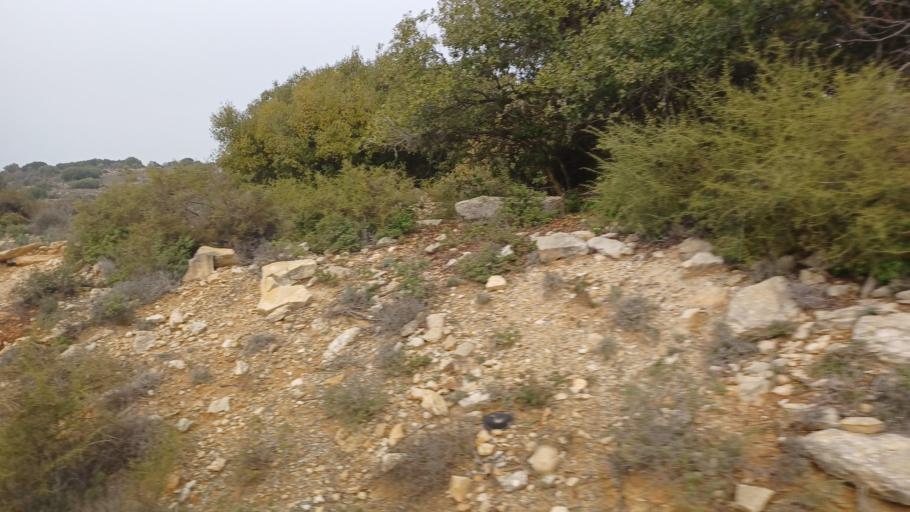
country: CY
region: Limassol
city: Pachna
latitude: 34.7639
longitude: 32.7559
